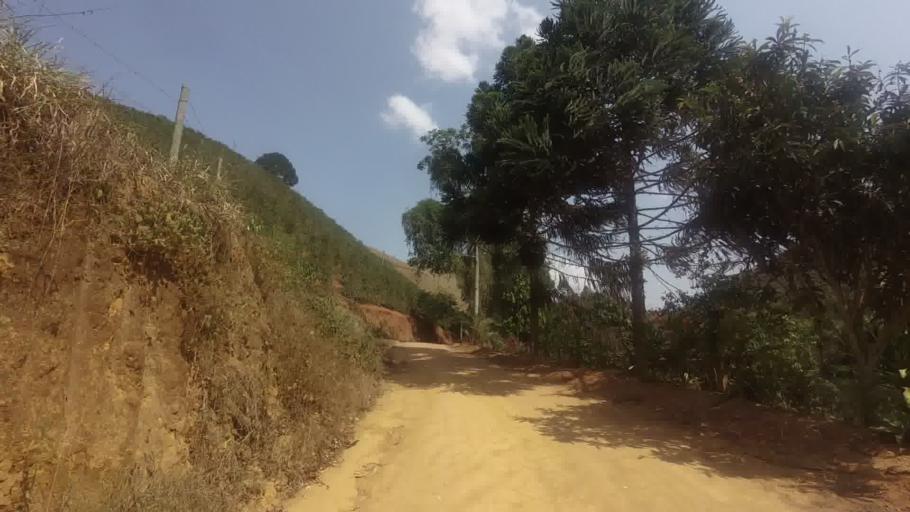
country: BR
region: Espirito Santo
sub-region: Mimoso Do Sul
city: Mimoso do Sul
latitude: -20.9897
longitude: -41.4998
